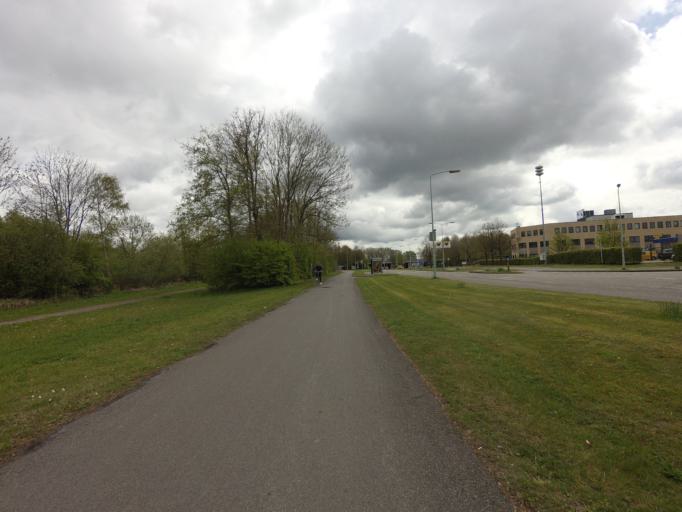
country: NL
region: North Holland
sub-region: Gemeente Naarden
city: Naarden
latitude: 52.3080
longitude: 5.1439
